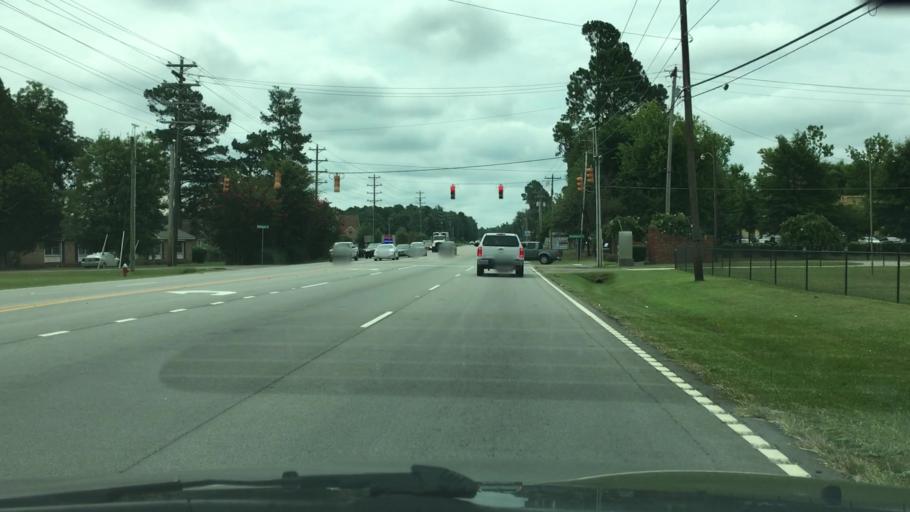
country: US
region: South Carolina
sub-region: Aiken County
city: Aiken
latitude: 33.5044
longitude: -81.7085
